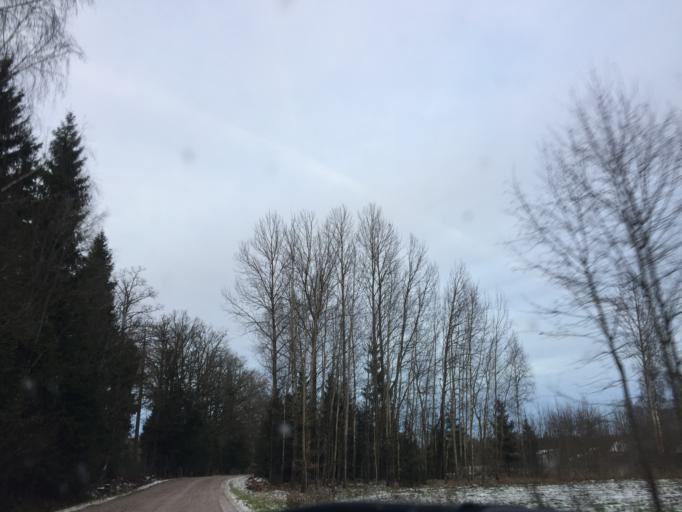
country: LV
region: Limbazu Rajons
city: Limbazi
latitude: 57.5582
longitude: 24.8163
